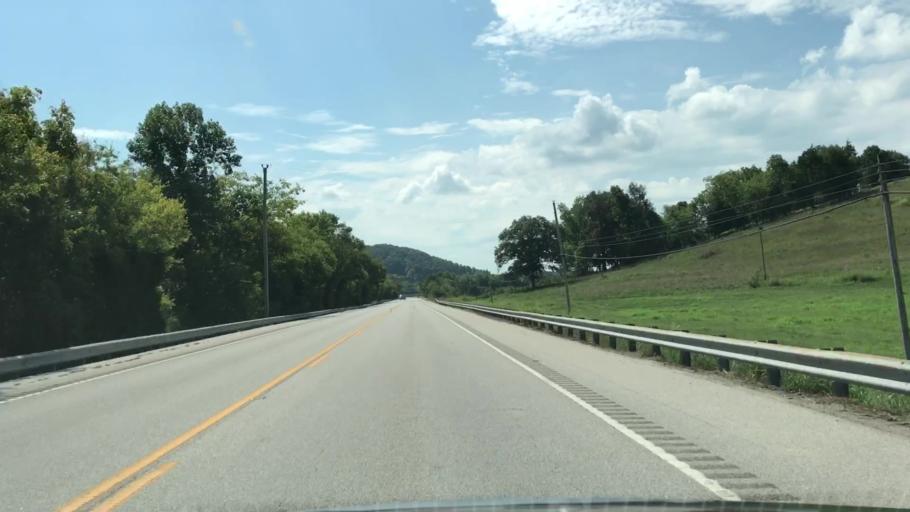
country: US
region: Tennessee
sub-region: Smith County
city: Carthage
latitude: 36.3133
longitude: -86.0093
